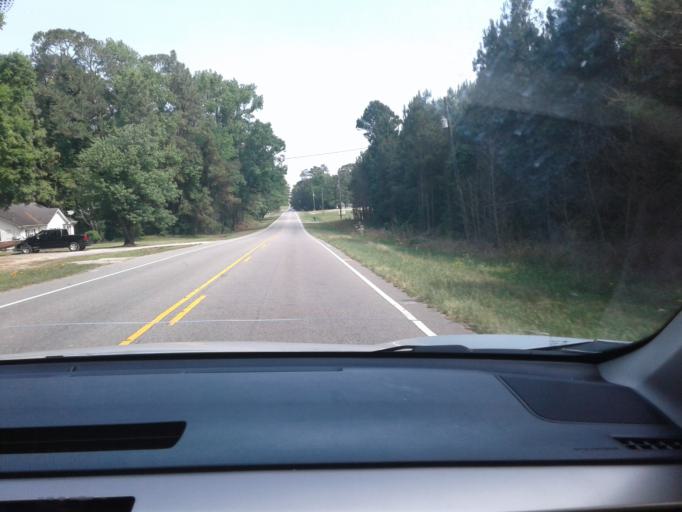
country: US
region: North Carolina
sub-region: Harnett County
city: Coats
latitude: 35.4267
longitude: -78.6773
